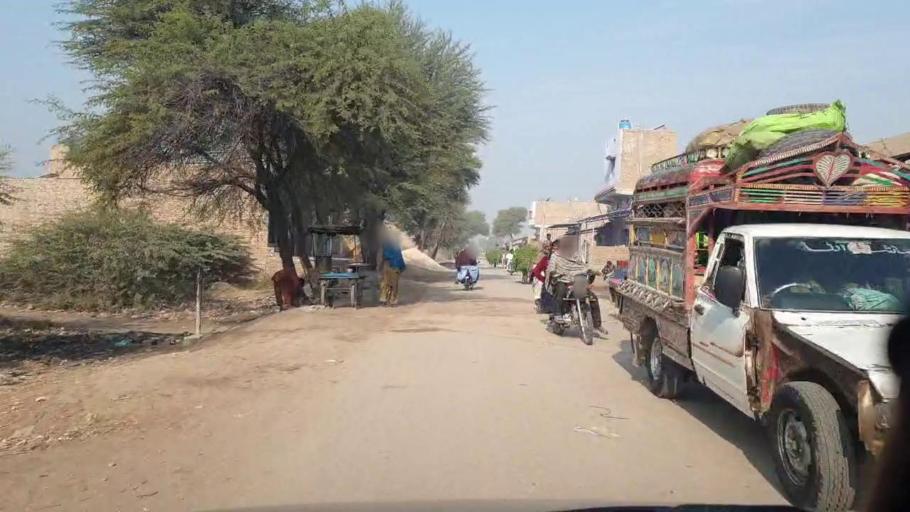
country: PK
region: Sindh
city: Shahdadpur
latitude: 25.9308
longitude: 68.6135
